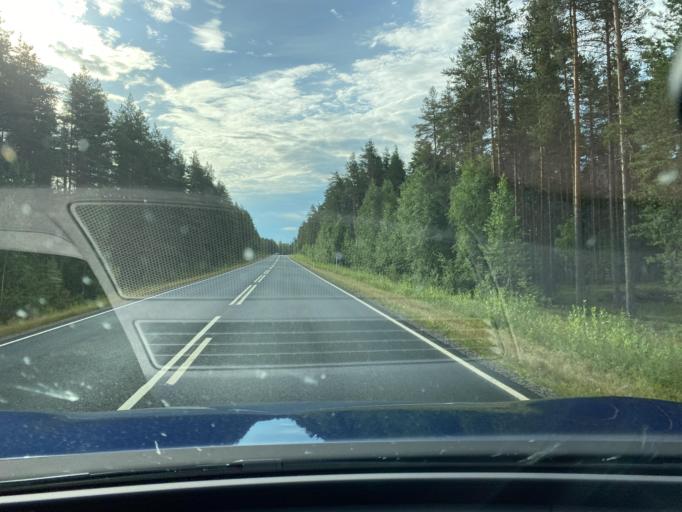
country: FI
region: Central Ostrobothnia
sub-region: Kaustinen
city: Veteli
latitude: 63.4096
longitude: 23.9668
